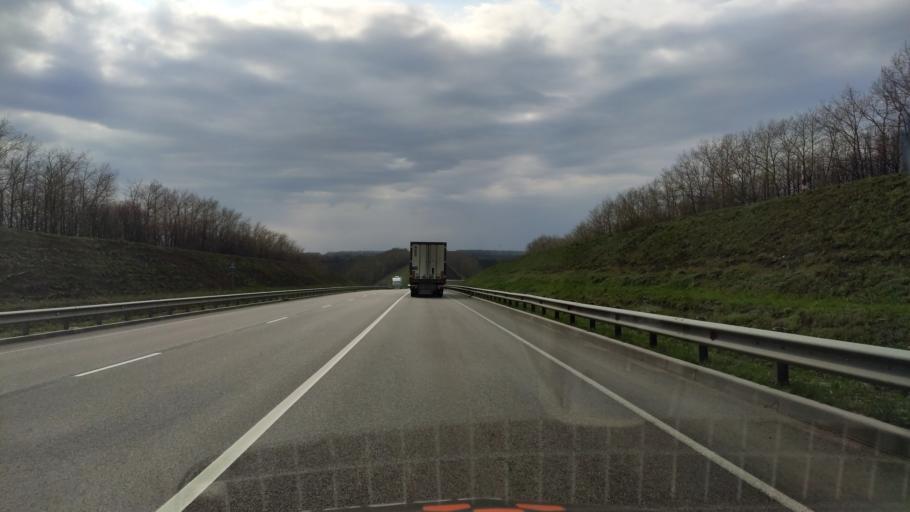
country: RU
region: Voronezj
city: Nizhnedevitsk
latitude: 51.5592
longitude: 38.2431
